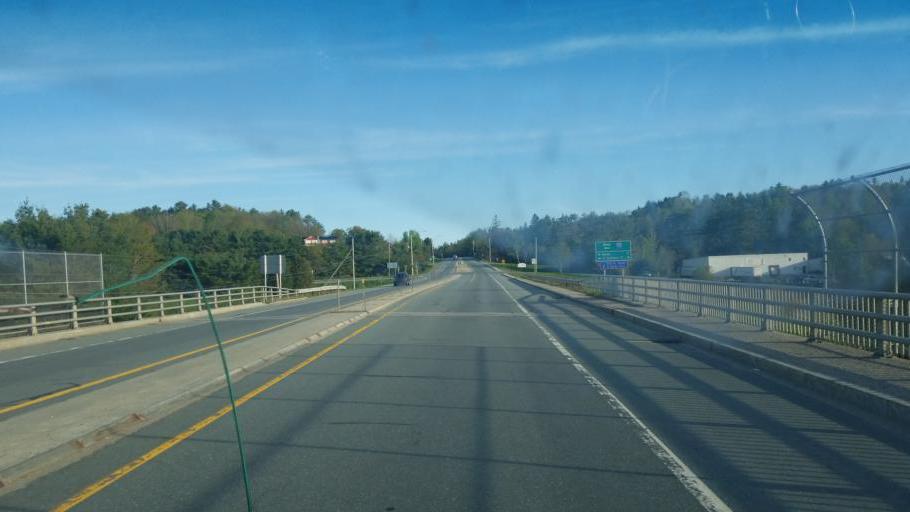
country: US
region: New Hampshire
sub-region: Grafton County
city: Littleton
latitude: 44.3254
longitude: -71.8061
